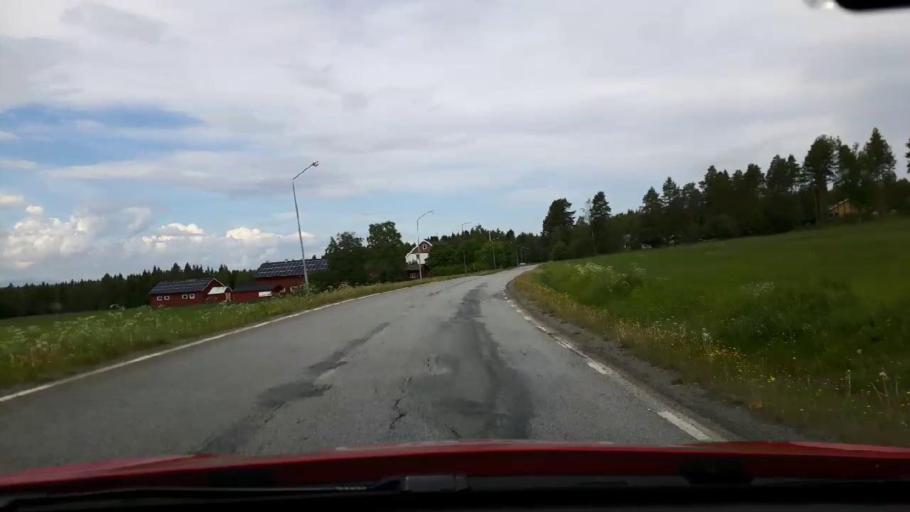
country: SE
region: Jaemtland
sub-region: Bergs Kommun
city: Hoverberg
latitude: 63.0225
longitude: 14.4784
